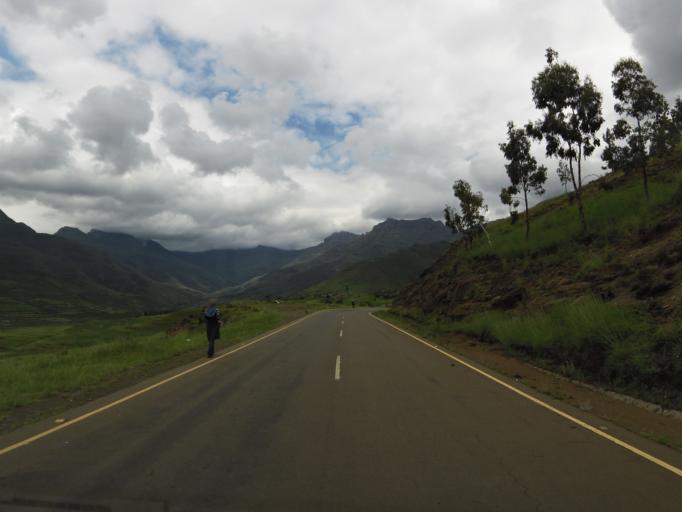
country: LS
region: Butha-Buthe
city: Butha-Buthe
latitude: -29.0373
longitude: 28.3024
